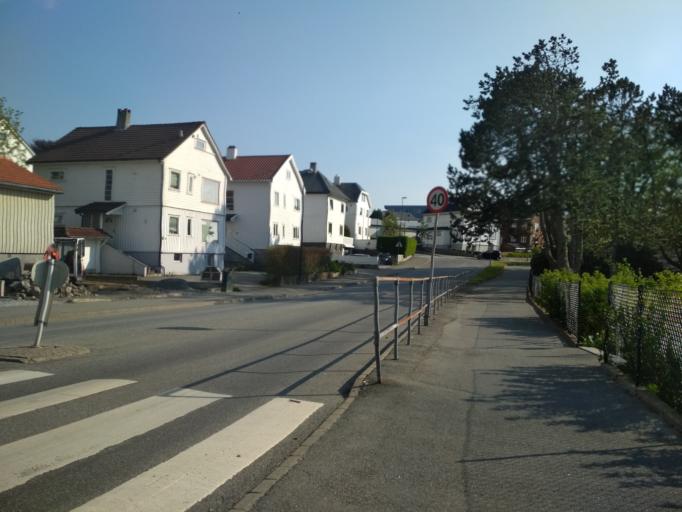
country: NO
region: Rogaland
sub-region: Stavanger
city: Stavanger
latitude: 58.9684
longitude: 5.7115
